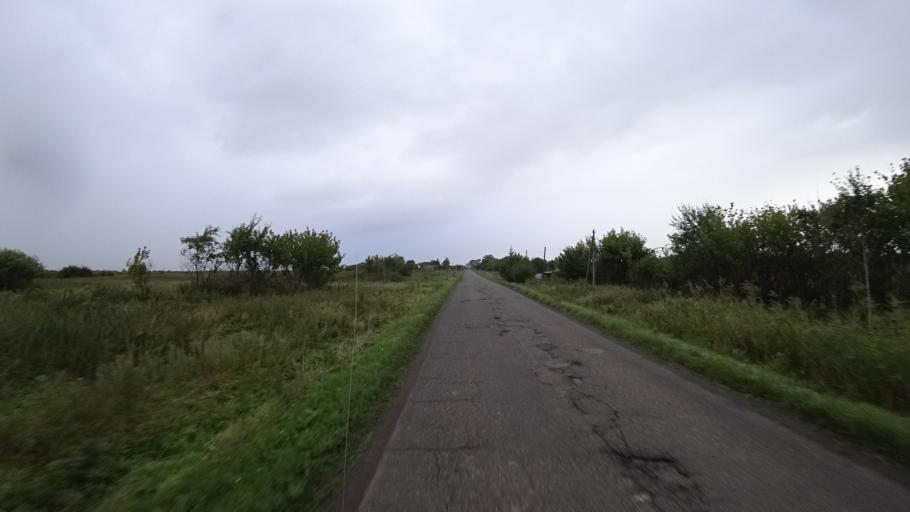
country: RU
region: Primorskiy
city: Chernigovka
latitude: 44.3947
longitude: 132.5282
